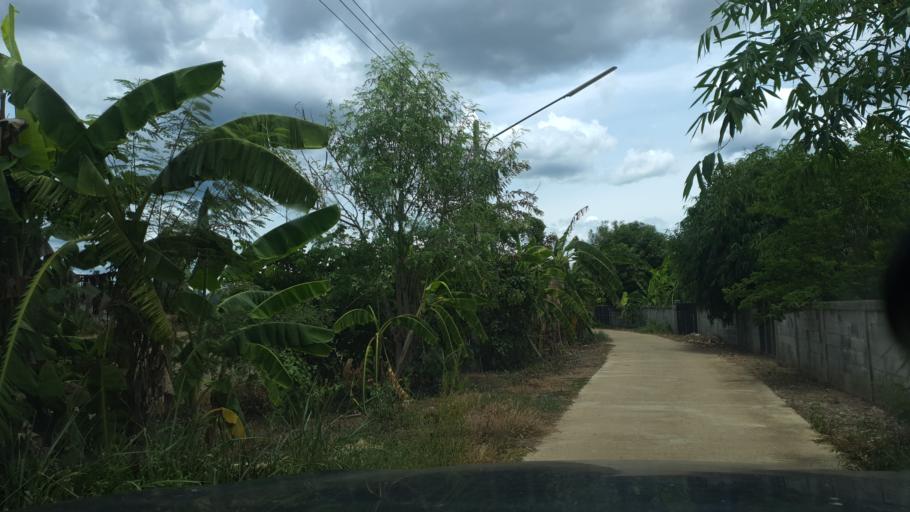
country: TH
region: Sukhothai
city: Thung Saliam
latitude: 17.3132
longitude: 99.5672
